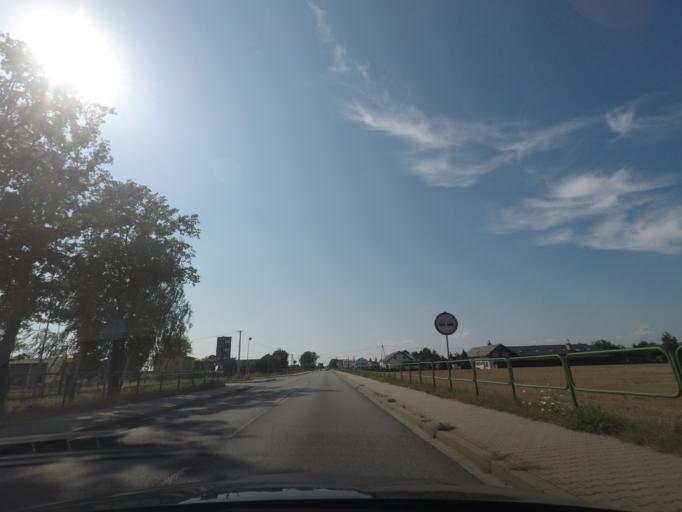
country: PL
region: Silesian Voivodeship
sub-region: Powiat pszczynski
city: Suszec
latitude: 50.0319
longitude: 18.7816
